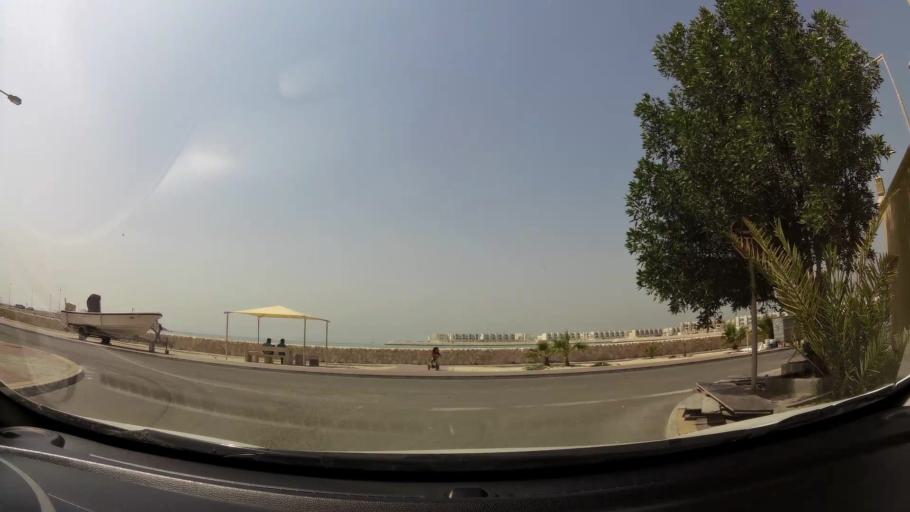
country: BH
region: Manama
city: Jidd Hafs
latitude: 26.2160
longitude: 50.4455
